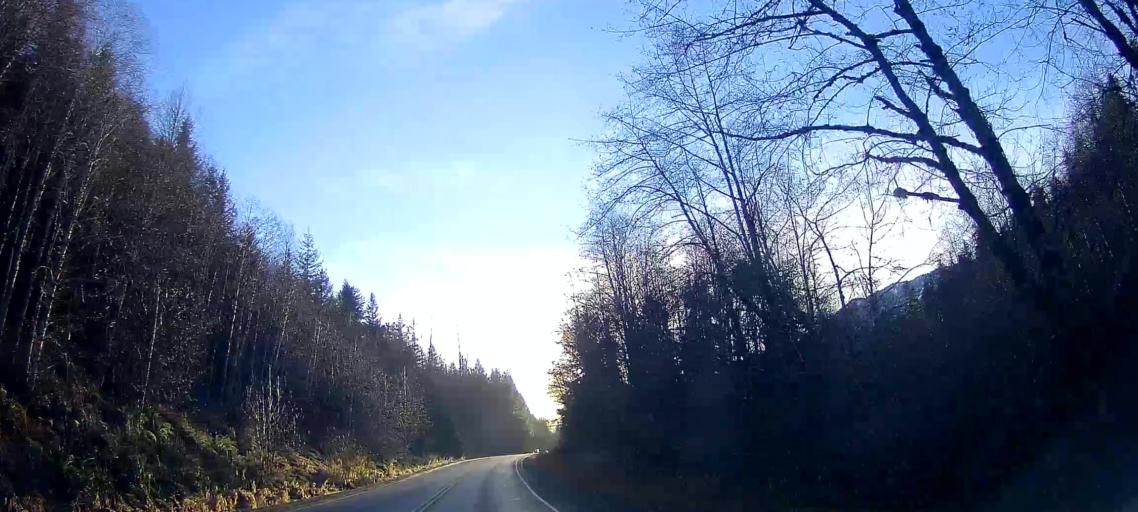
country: US
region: Washington
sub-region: Snohomish County
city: Darrington
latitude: 48.6195
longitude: -121.7493
